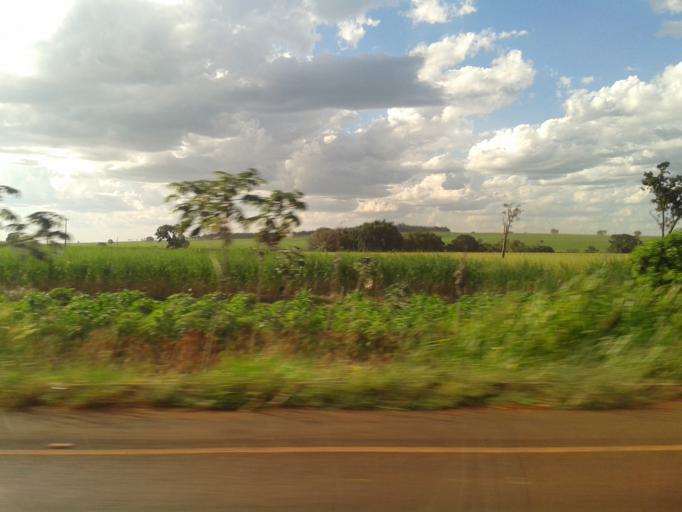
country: BR
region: Minas Gerais
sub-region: Santa Vitoria
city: Santa Vitoria
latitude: -18.6927
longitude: -49.9121
